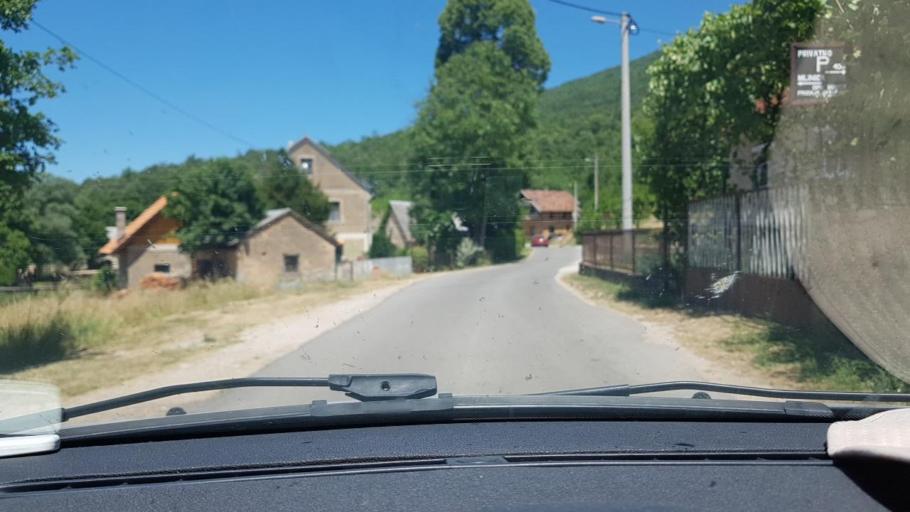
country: HR
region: Licko-Senjska
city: Otocac
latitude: 44.8140
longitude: 15.3592
